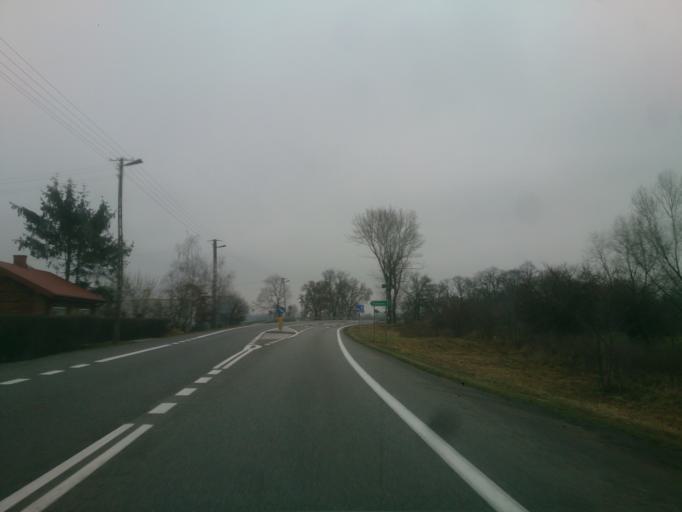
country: PL
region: Masovian Voivodeship
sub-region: Powiat plonski
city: Dzierzaznia
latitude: 52.6273
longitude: 20.2489
